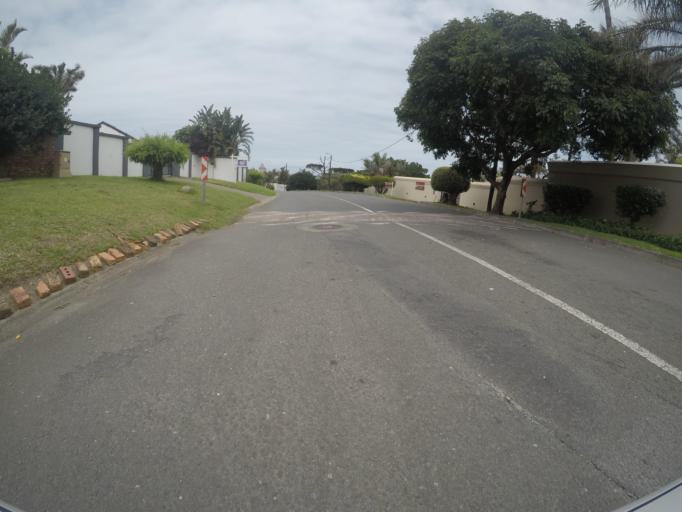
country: ZA
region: Eastern Cape
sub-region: Buffalo City Metropolitan Municipality
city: East London
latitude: -32.9799
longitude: 27.9484
